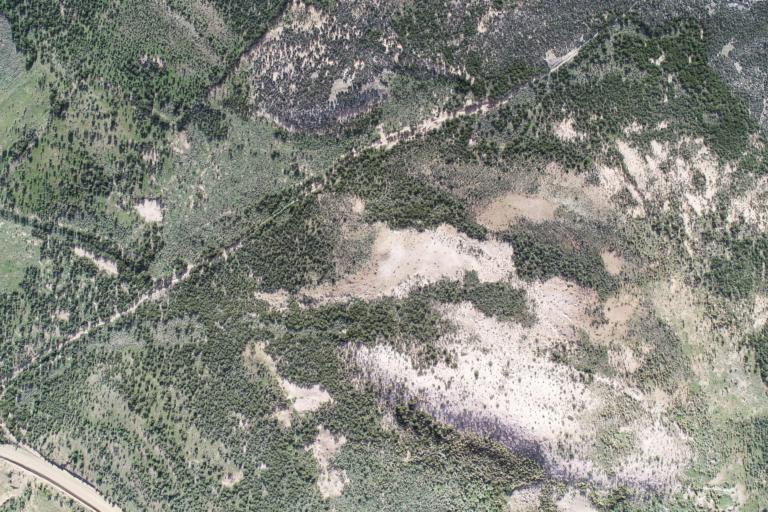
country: BO
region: La Paz
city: Patacamaya
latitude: -17.2962
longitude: -68.4878
